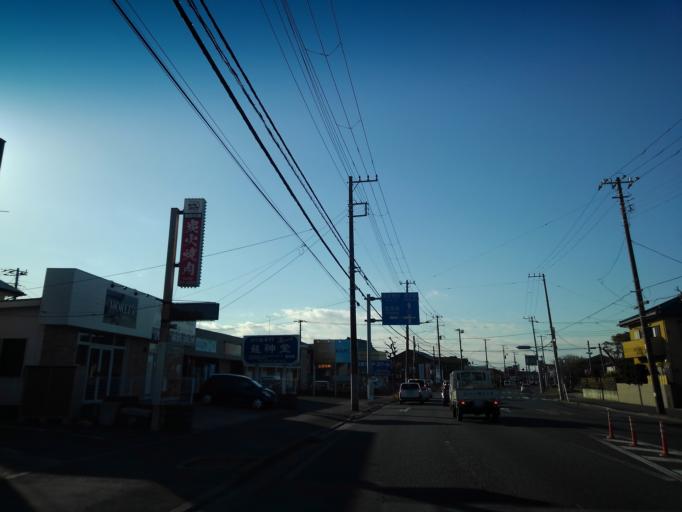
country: JP
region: Chiba
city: Kimitsu
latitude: 35.3292
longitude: 139.8983
